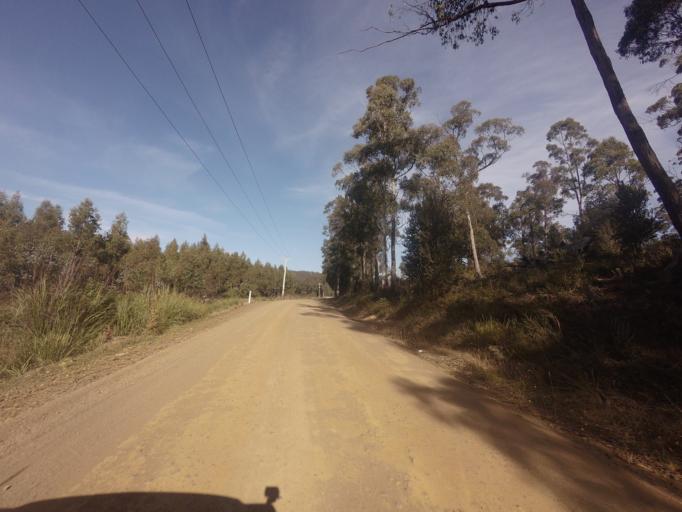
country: AU
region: Tasmania
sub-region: Sorell
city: Sorell
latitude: -42.4953
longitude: 147.5275
